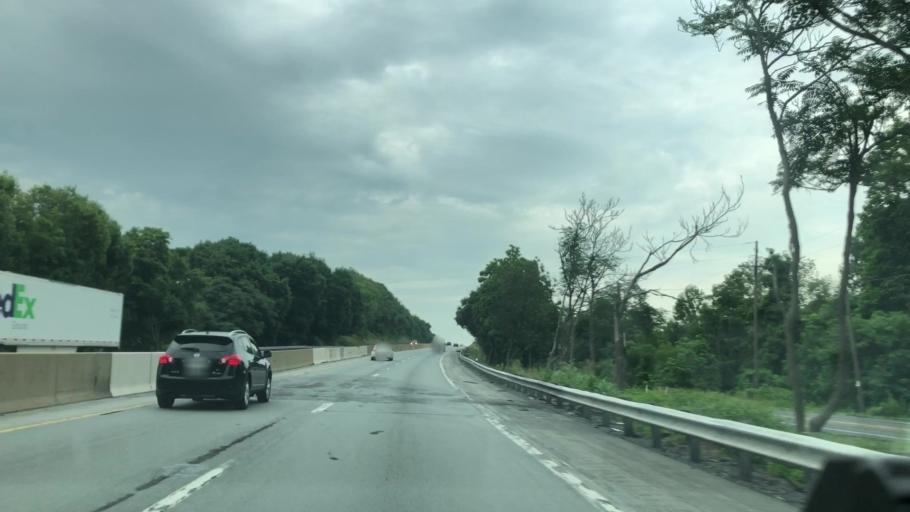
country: US
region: Pennsylvania
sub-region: Berks County
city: Kutztown
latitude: 40.5792
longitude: -75.8428
